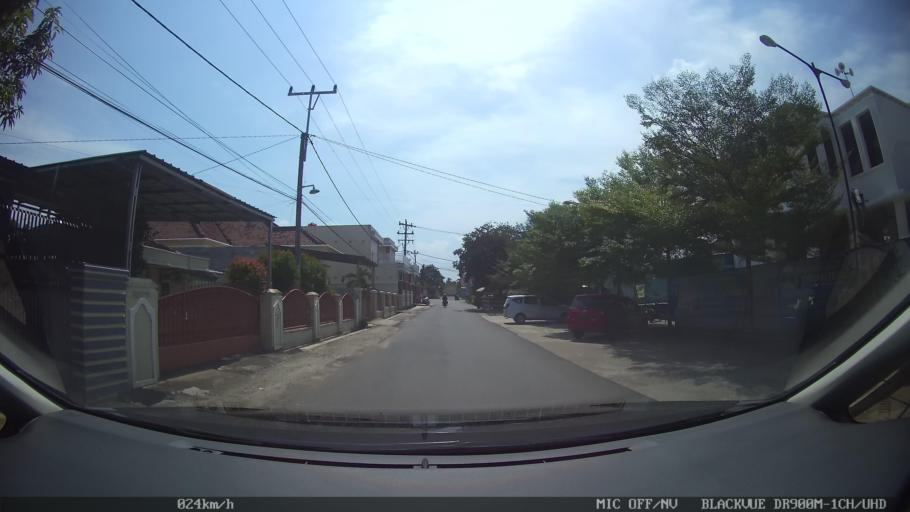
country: ID
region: Lampung
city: Kedaton
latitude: -5.3606
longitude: 105.2516
